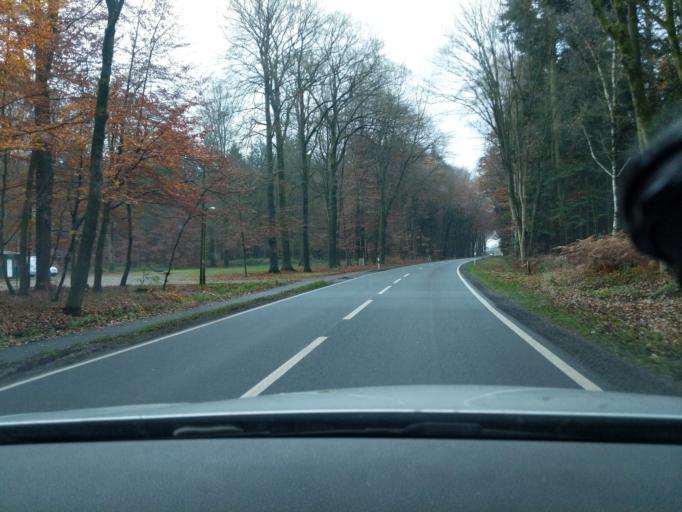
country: DE
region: Lower Saxony
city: Heeslingen
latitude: 53.3307
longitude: 9.3600
